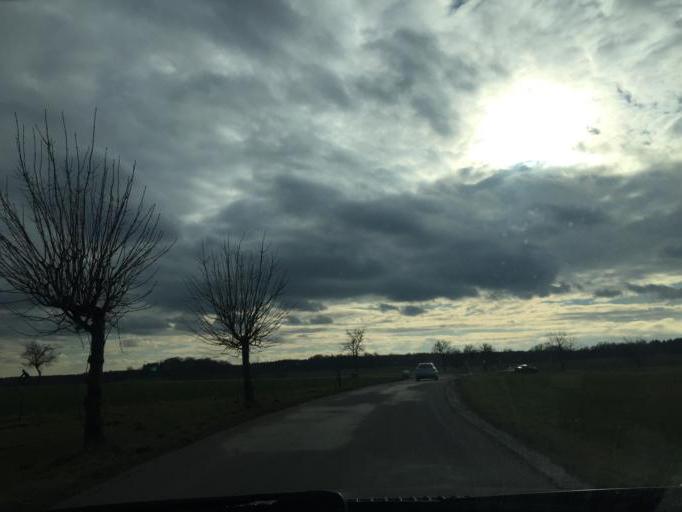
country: DE
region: Saxony
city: Ebersbach
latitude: 51.1999
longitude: 13.6694
